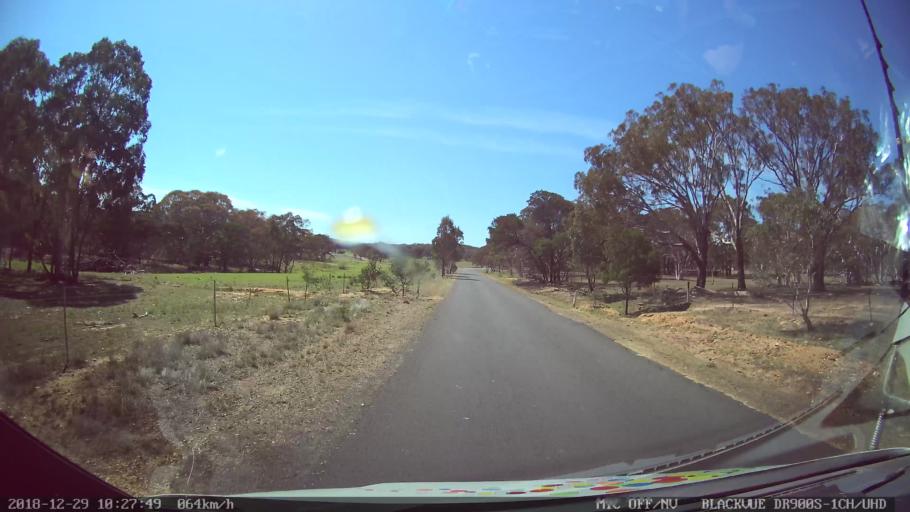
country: AU
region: New South Wales
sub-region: Yass Valley
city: Gundaroo
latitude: -34.9376
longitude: 149.4521
